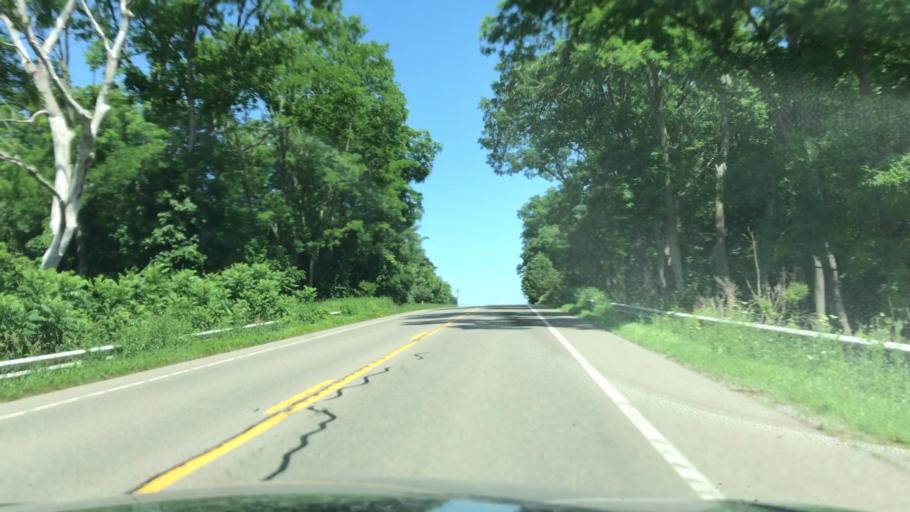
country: US
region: New York
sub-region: Livingston County
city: Mount Morris
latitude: 42.7562
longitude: -77.8954
